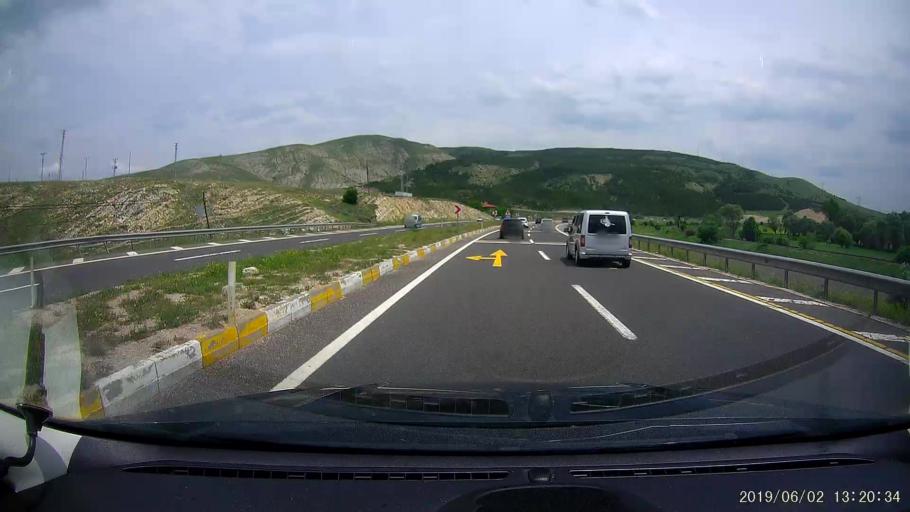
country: TR
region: Cankiri
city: Cerkes
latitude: 40.8417
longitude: 32.7627
